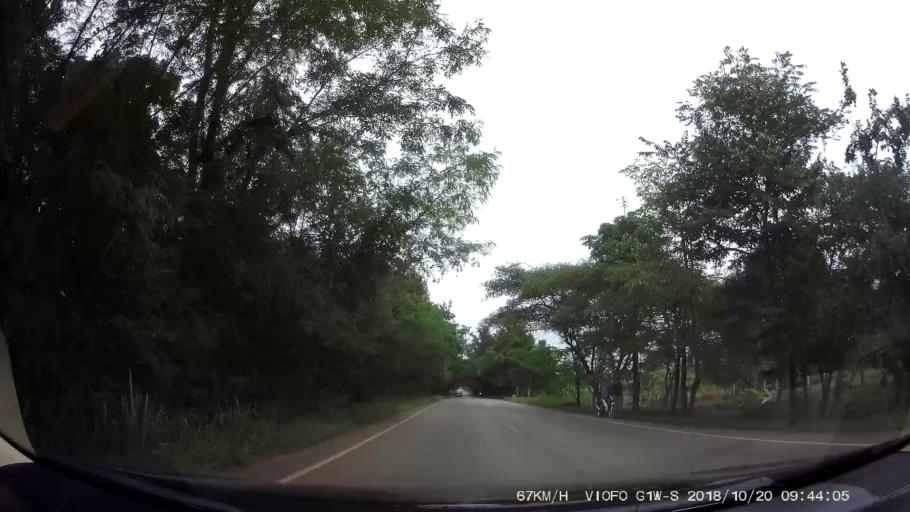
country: TH
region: Chaiyaphum
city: Khon San
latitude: 16.4796
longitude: 101.9455
